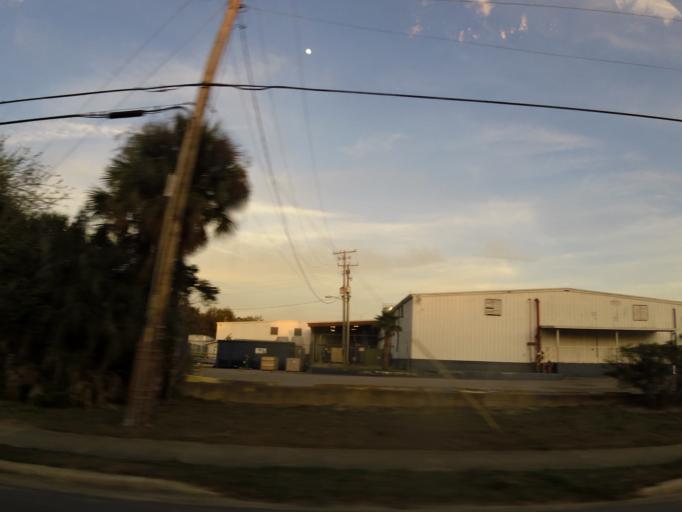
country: US
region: Florida
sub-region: Volusia County
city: North DeLand
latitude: 29.0689
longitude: -81.3046
